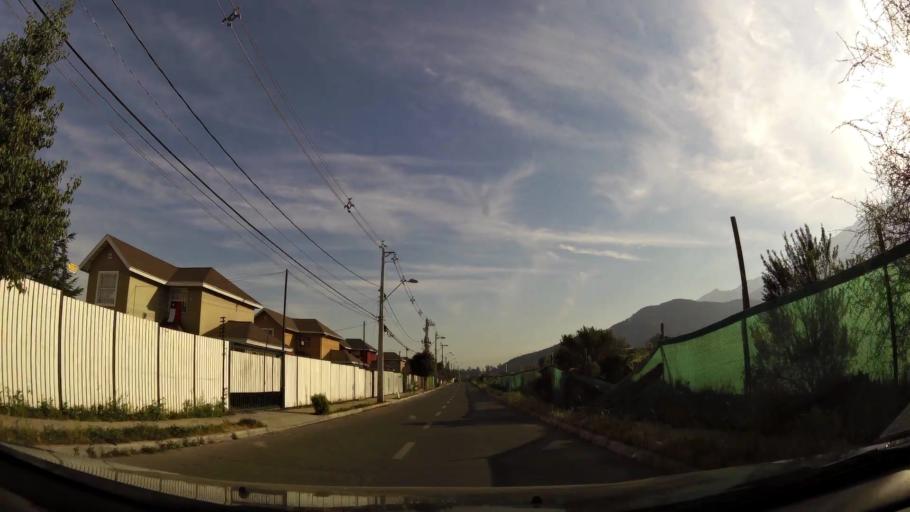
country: CL
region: Santiago Metropolitan
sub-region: Provincia de Cordillera
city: Puente Alto
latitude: -33.5654
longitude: -70.5437
